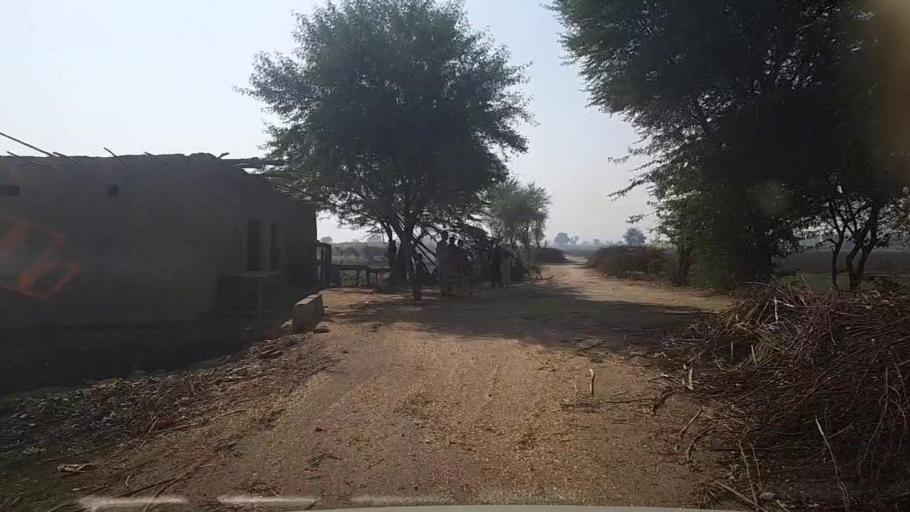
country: PK
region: Sindh
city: Kandiari
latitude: 26.9966
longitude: 68.4911
